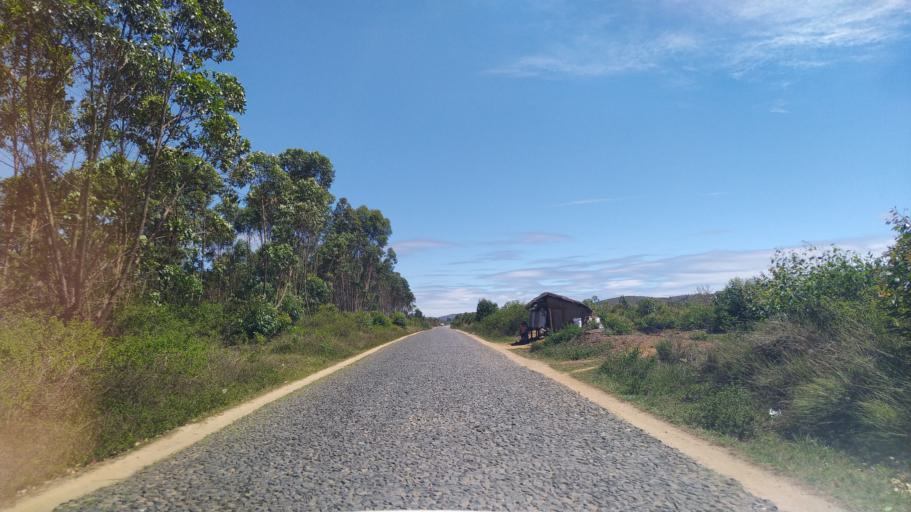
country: MG
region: Alaotra Mangoro
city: Moramanga
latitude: -18.7740
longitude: 48.2502
